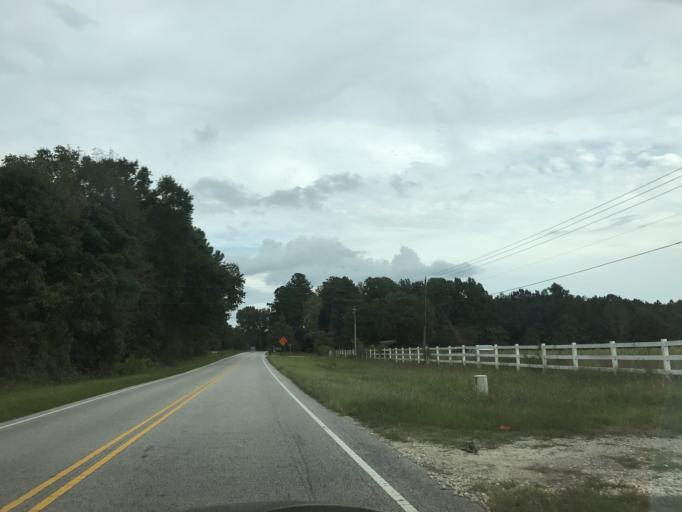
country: US
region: North Carolina
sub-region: Franklin County
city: Youngsville
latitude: 36.0026
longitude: -78.4299
